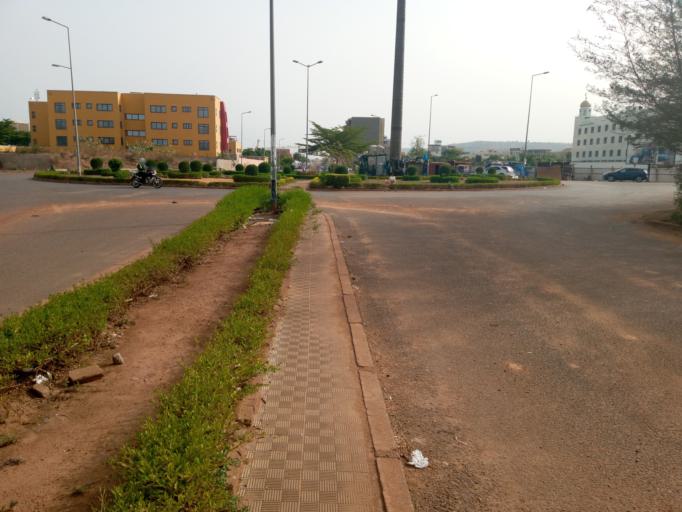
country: ML
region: Bamako
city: Bamako
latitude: 12.6305
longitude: -8.0270
